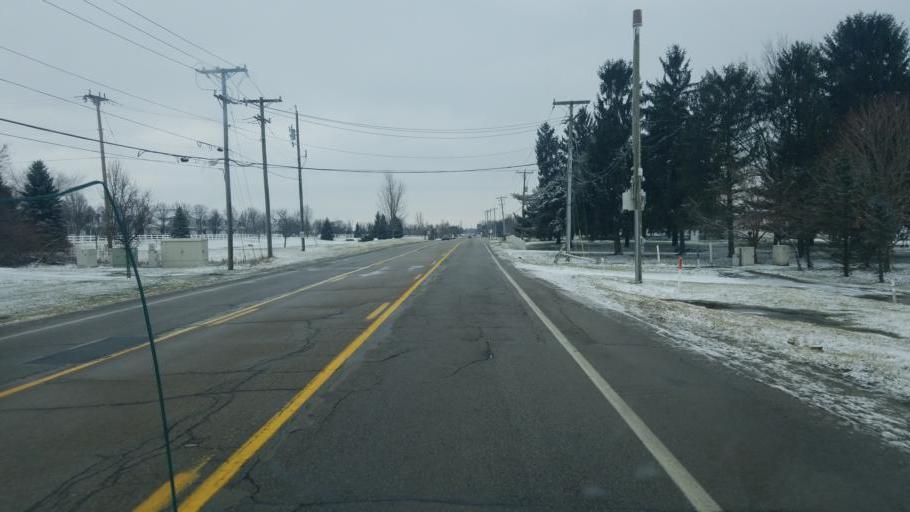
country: US
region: Ohio
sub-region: Franklin County
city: Reynoldsburg
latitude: 40.0150
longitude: -82.7901
